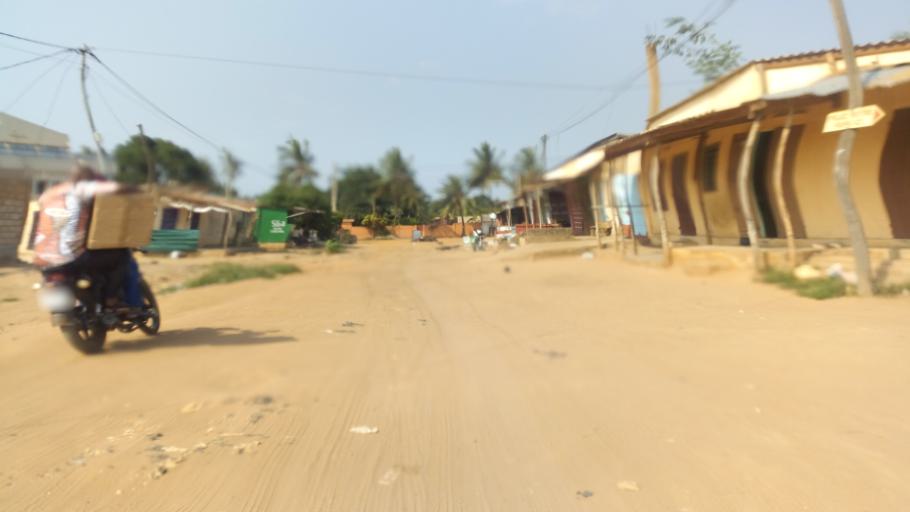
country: TG
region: Maritime
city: Lome
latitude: 6.1904
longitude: 1.1822
